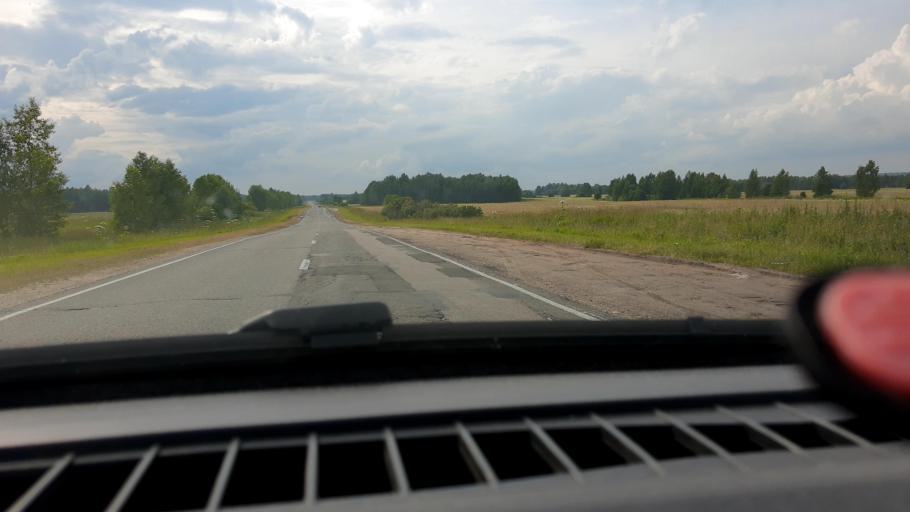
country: RU
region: Nizjnij Novgorod
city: Sitniki
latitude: 56.4990
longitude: 43.9957
